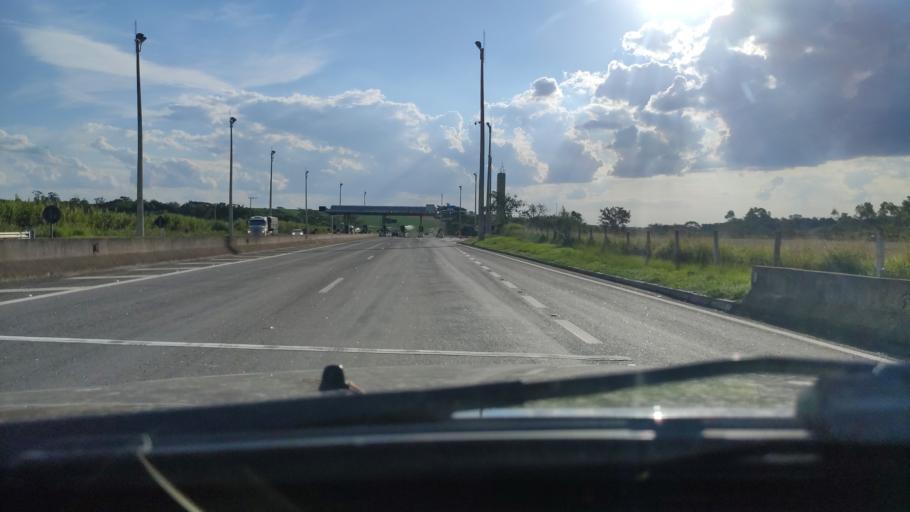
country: BR
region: Sao Paulo
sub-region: Mogi-Mirim
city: Mogi Mirim
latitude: -22.4565
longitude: -46.9004
